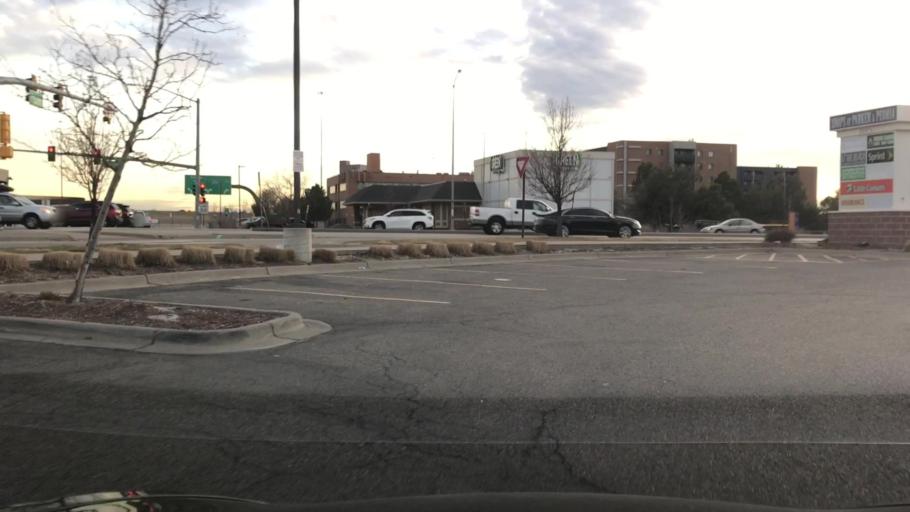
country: US
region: Colorado
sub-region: Adams County
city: Aurora
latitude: 39.6596
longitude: -104.8479
